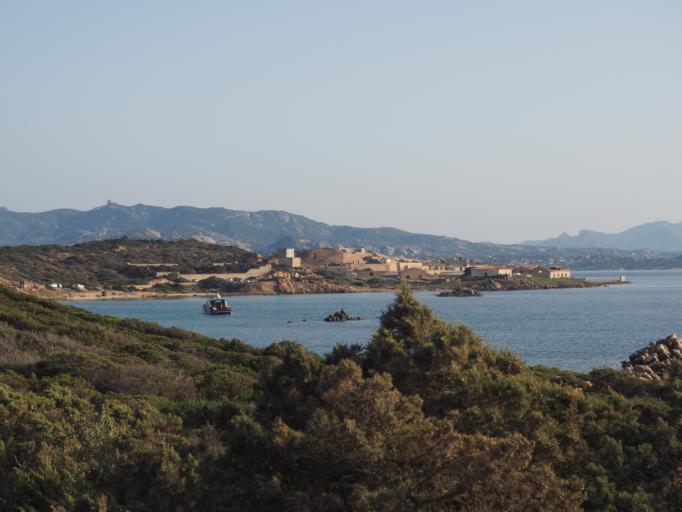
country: IT
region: Sardinia
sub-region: Provincia di Olbia-Tempio
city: La Maddalena
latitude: 41.1817
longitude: 9.4677
